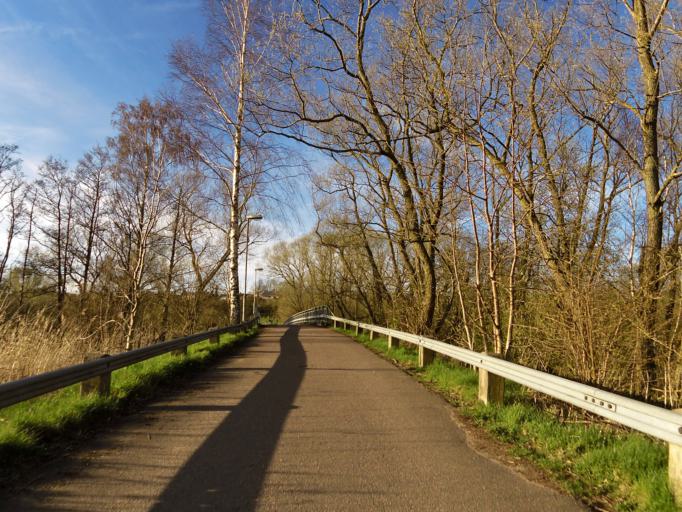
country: SE
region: Skane
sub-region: Kavlinge Kommun
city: Kaevlinge
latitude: 55.7860
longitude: 13.0909
